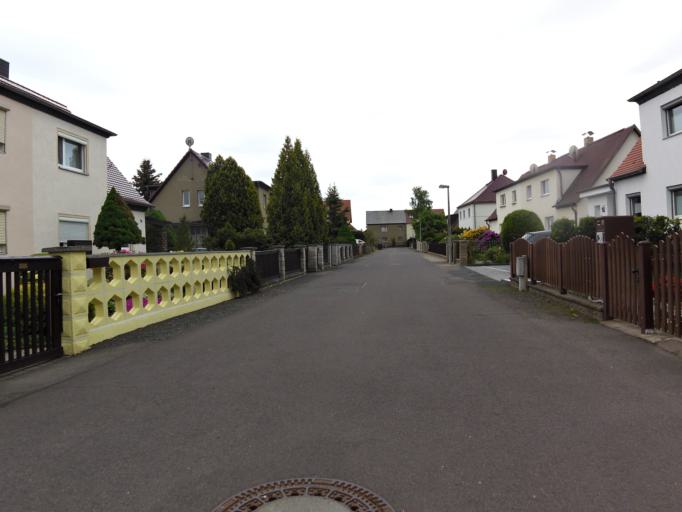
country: DE
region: Saxony
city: Markkleeberg
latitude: 51.2858
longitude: 12.3100
